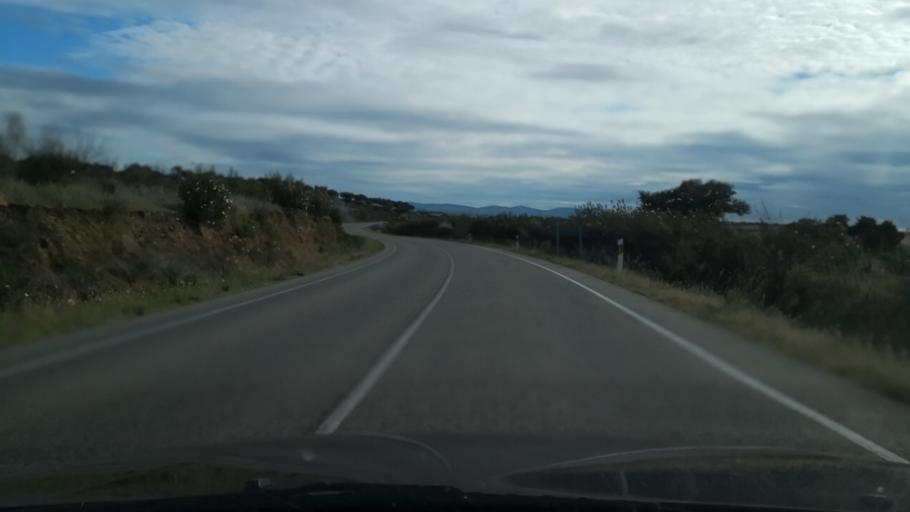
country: ES
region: Extremadura
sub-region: Provincia de Caceres
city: Moraleja
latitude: 40.1085
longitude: -6.6736
